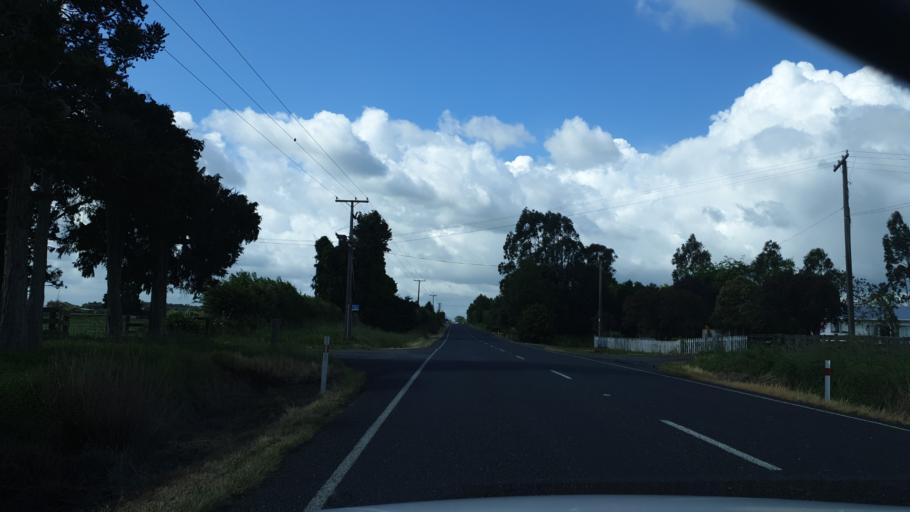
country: NZ
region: Waikato
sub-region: Hauraki District
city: Paeroa
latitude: -37.5094
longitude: 175.4959
